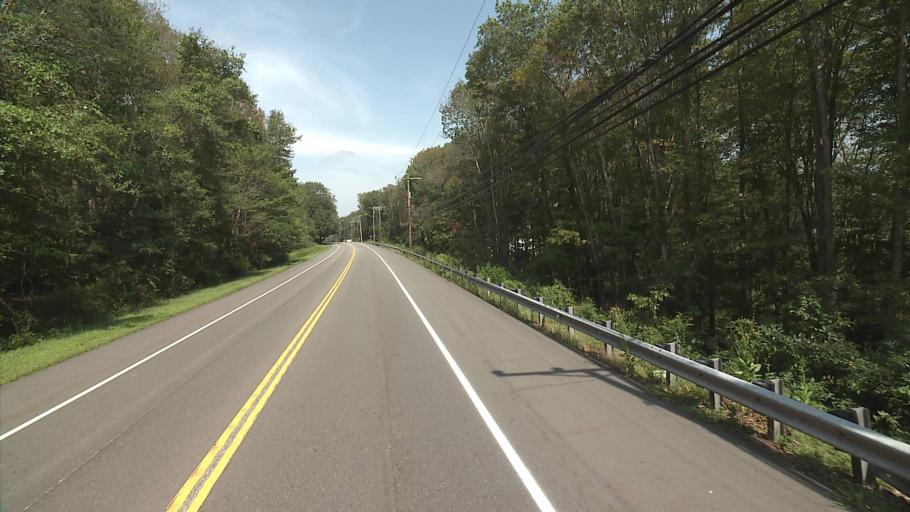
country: US
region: Connecticut
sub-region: New Haven County
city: Madison Center
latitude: 41.3495
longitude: -72.6324
